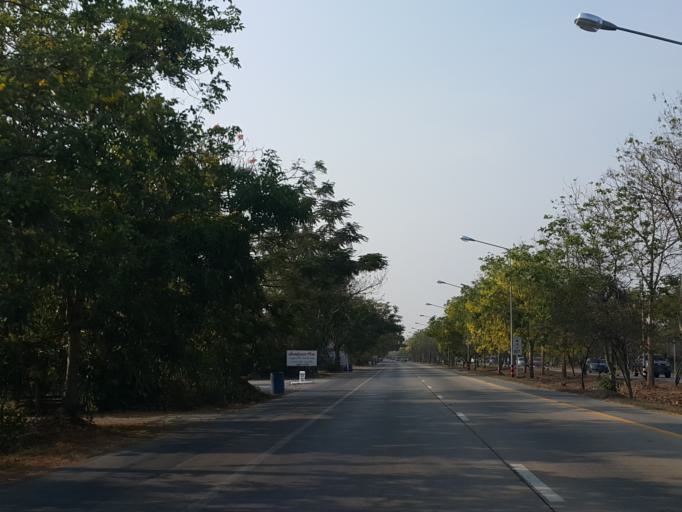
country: TH
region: Suphan Buri
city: Sam Chuk
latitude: 14.7756
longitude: 100.0904
